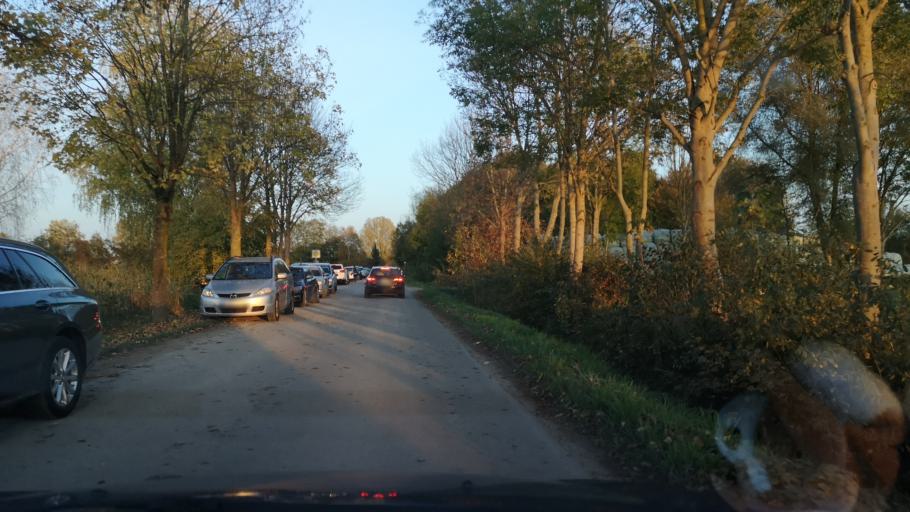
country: DE
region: Bavaria
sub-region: Upper Bavaria
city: Ismaning
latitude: 48.2454
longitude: 11.7328
